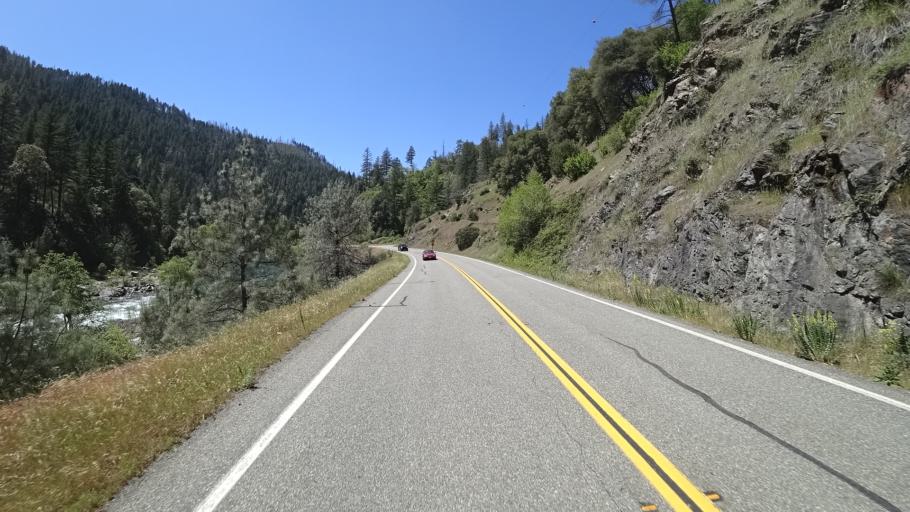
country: US
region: California
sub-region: Trinity County
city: Hayfork
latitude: 40.7619
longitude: -123.2835
